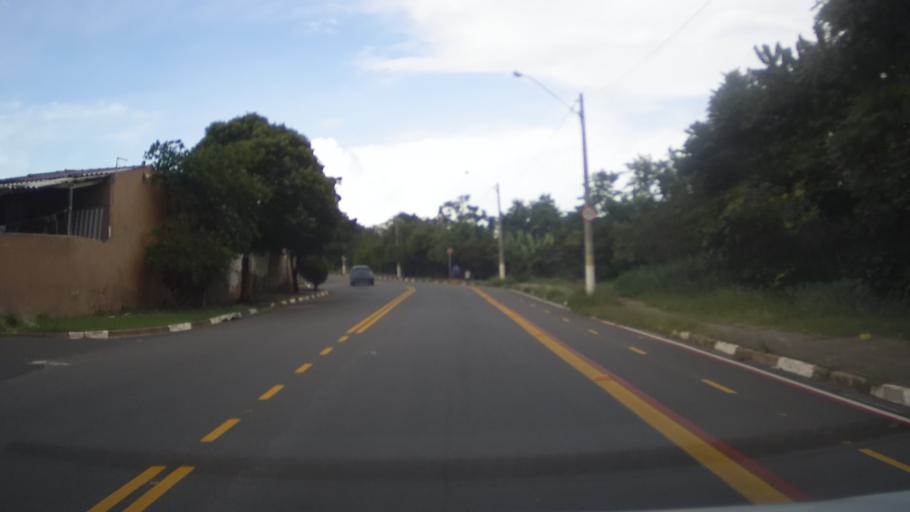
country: BR
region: Sao Paulo
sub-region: Hortolandia
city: Hortolandia
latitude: -22.9566
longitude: -47.1953
